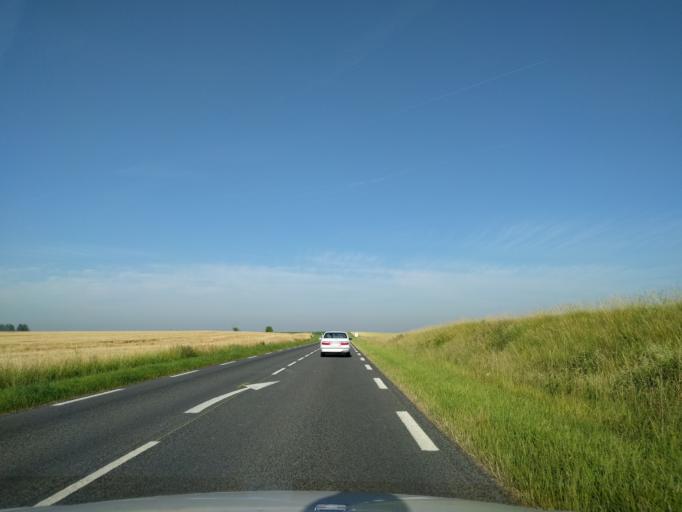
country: FR
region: Picardie
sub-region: Departement de la Somme
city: Montdidier
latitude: 49.6512
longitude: 2.6573
